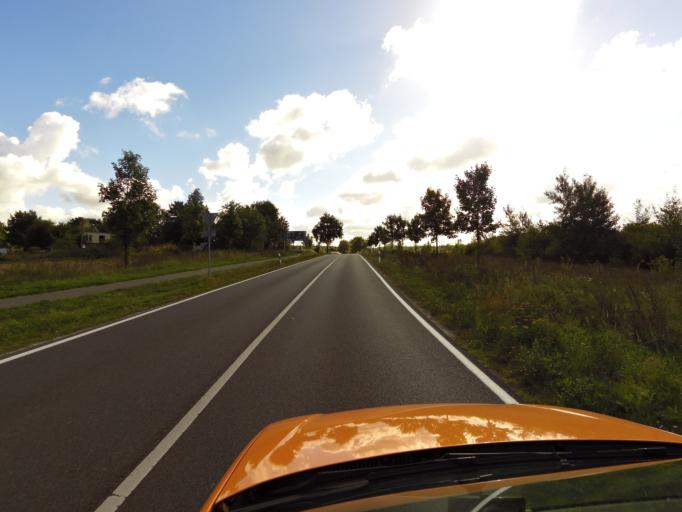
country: DE
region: Brandenburg
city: Michendorf
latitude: 52.3024
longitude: 13.0334
